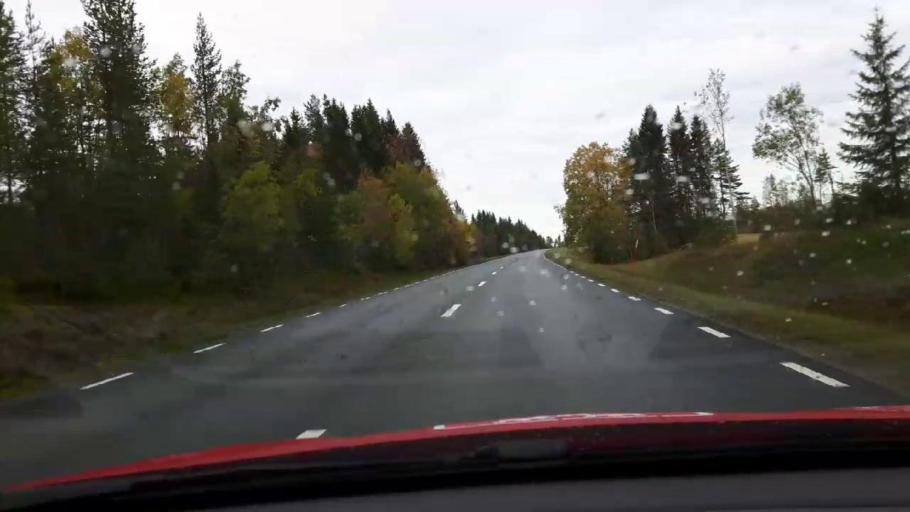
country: SE
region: Jaemtland
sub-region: Krokoms Kommun
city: Krokom
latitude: 63.1061
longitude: 14.2958
